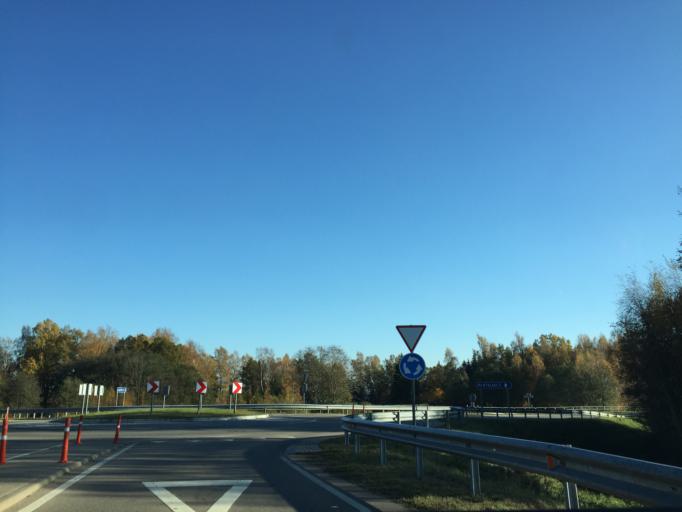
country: LT
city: Plateliai
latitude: 56.0710
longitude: 21.8229
